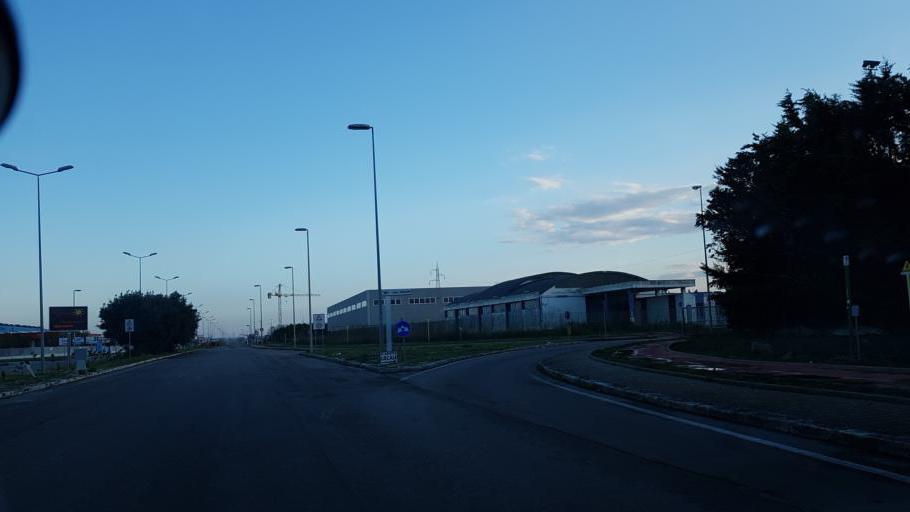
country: IT
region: Apulia
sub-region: Provincia di Lecce
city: Surbo
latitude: 40.3790
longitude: 18.1272
